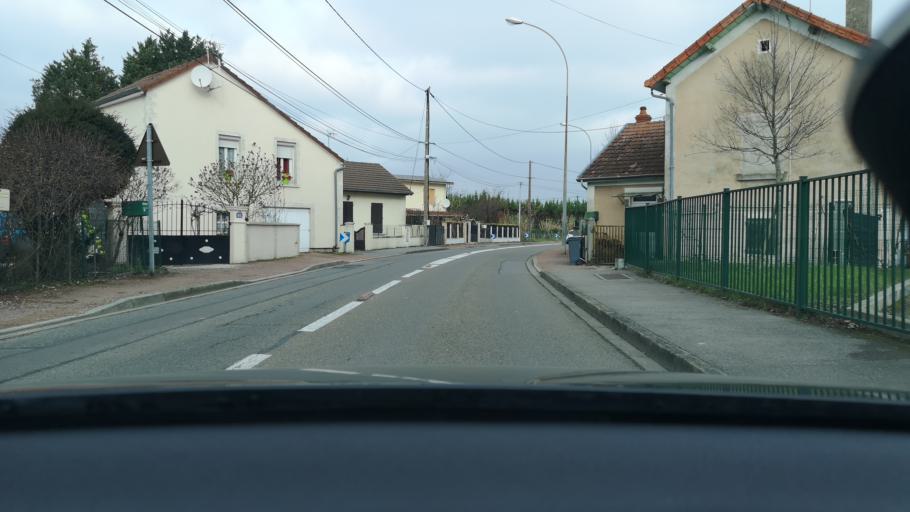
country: FR
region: Bourgogne
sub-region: Departement de Saone-et-Loire
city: Chalon-sur-Saone
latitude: 46.8024
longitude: 4.8507
